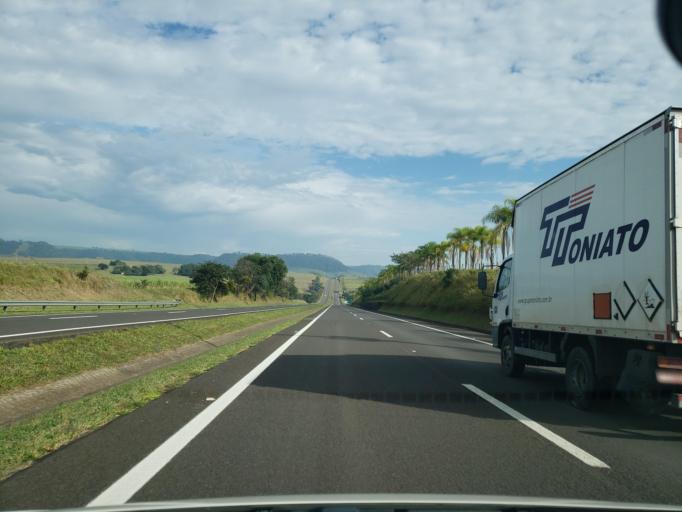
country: BR
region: Sao Paulo
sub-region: Dois Corregos
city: Dois Corregos
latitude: -22.2447
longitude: -48.3061
